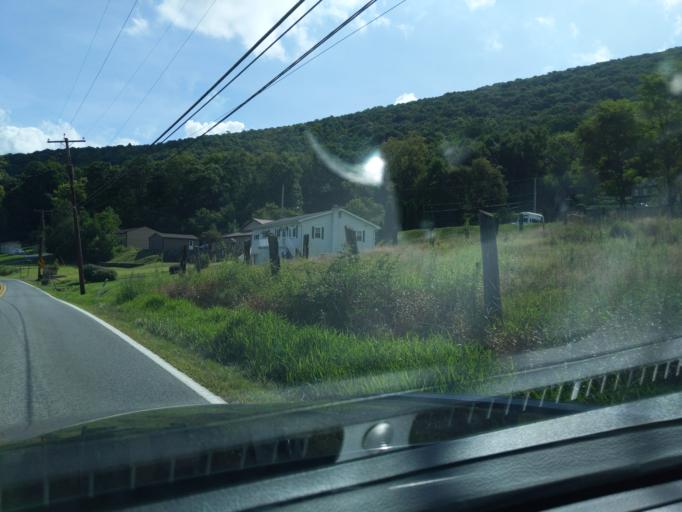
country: US
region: Pennsylvania
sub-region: Blair County
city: Hollidaysburg
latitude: 40.4080
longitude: -78.3777
